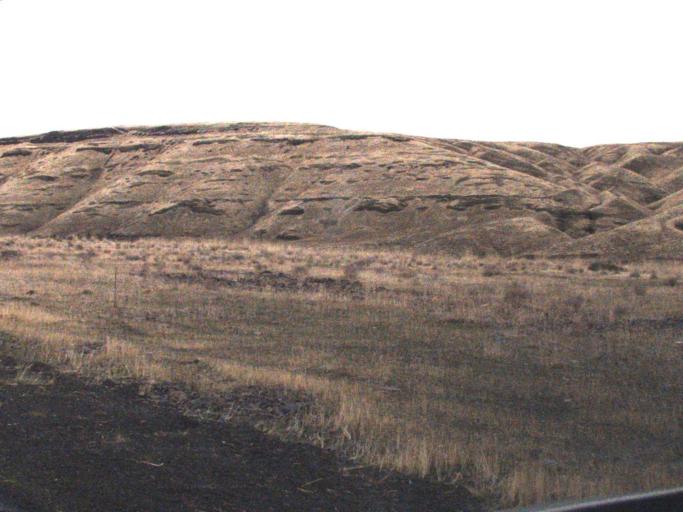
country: US
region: Washington
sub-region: Walla Walla County
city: Waitsburg
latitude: 46.5631
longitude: -118.1854
